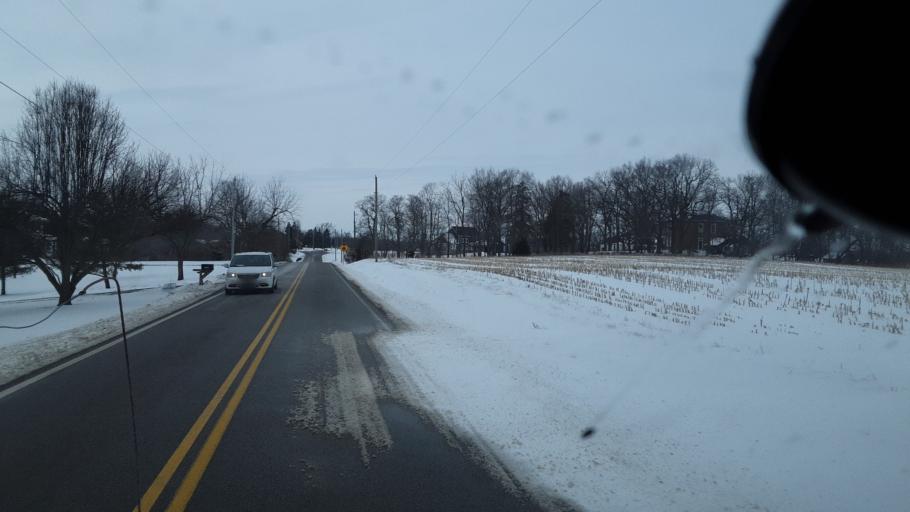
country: US
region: Ohio
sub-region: Madison County
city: Plain City
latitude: 40.1425
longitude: -83.3322
